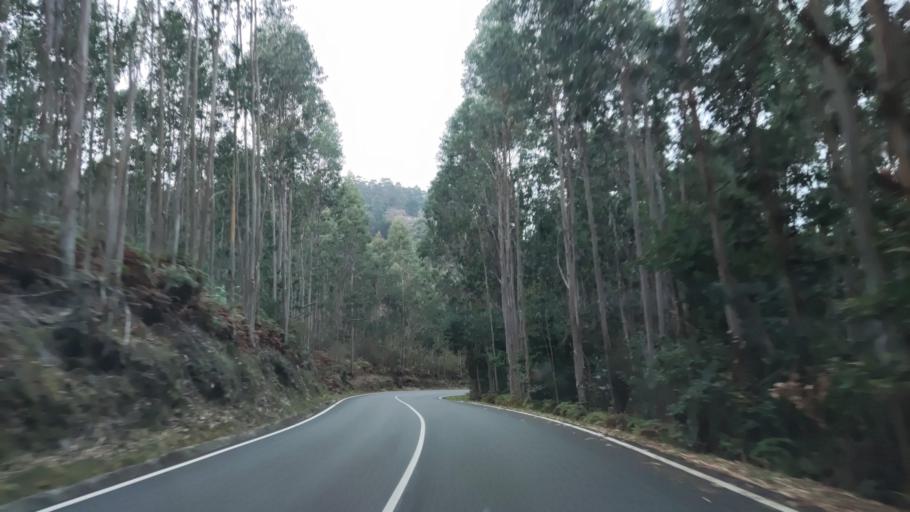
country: ES
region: Galicia
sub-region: Provincia de Pontevedra
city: Catoira
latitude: 42.6594
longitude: -8.7507
